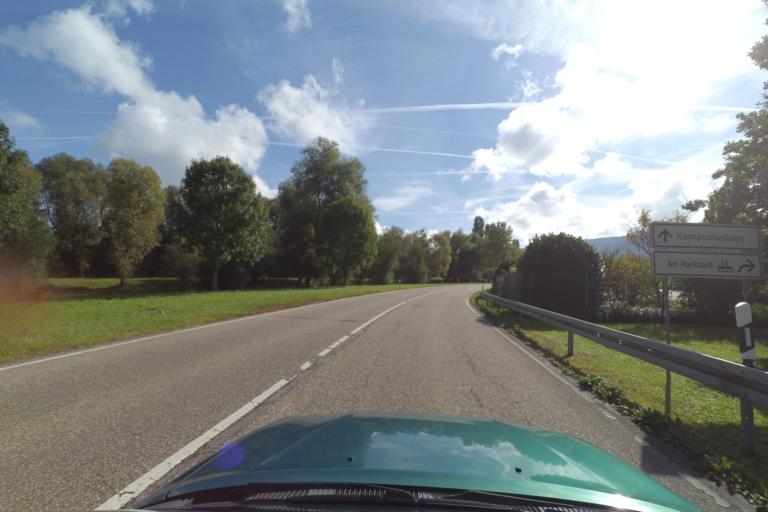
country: DE
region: Baden-Wuerttemberg
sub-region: Karlsruhe Region
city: Sinzheim
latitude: 48.7799
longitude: 8.1745
